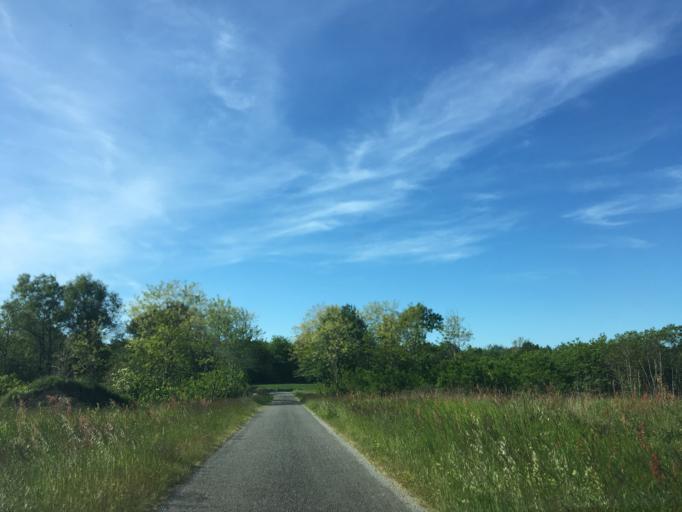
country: FR
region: Poitou-Charentes
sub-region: Departement de la Charente-Maritime
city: Mirambeau
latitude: 45.3386
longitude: -0.5817
